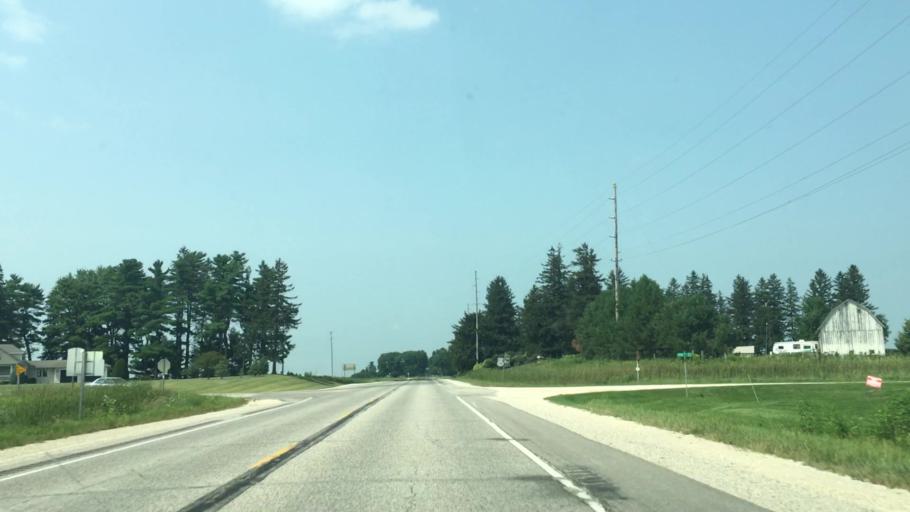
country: US
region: Iowa
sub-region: Fayette County
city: West Union
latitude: 42.9057
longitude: -91.8116
